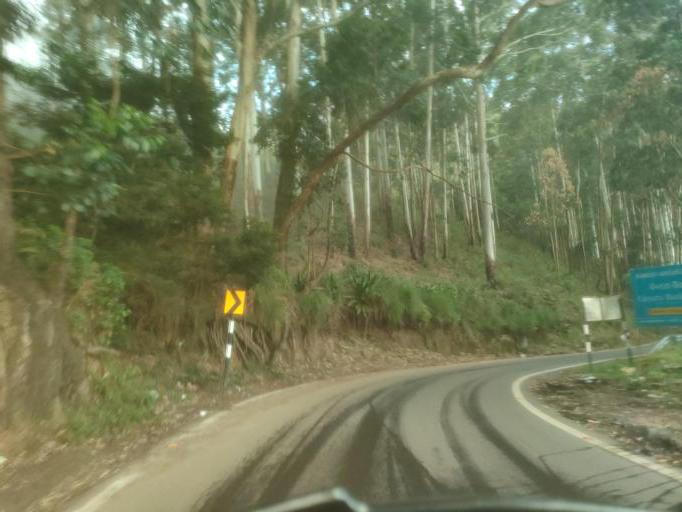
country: IN
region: Tamil Nadu
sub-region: Dindigul
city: Kodaikanal
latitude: 10.3143
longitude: 77.5663
